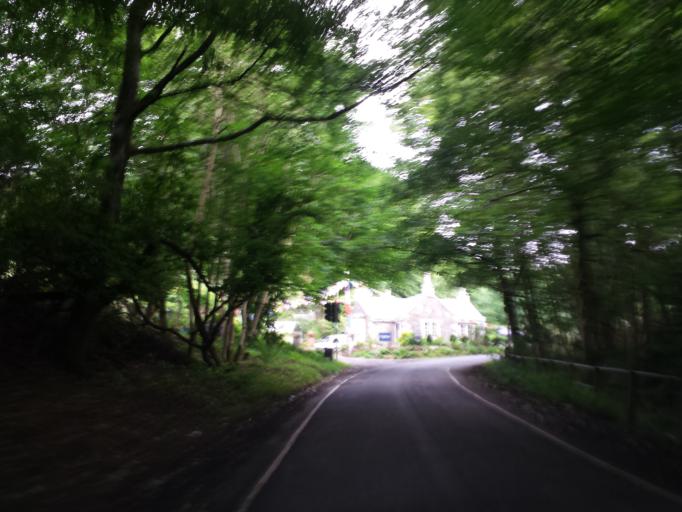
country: GB
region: Scotland
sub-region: Dumfries and Galloway
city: Moffat
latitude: 55.3325
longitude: -3.3942
